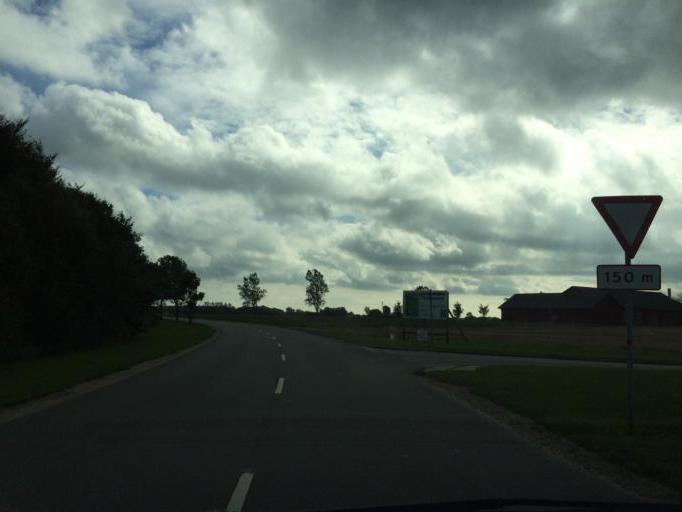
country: DK
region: North Denmark
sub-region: Bronderslev Kommune
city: Dronninglund
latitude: 57.1498
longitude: 10.2833
